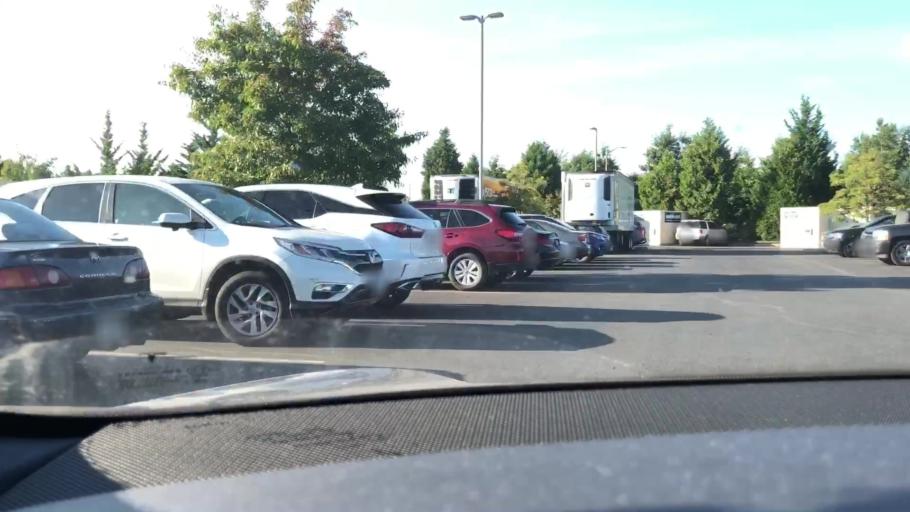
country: US
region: Washington
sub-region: Snohomish County
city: Marysville
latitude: 48.0900
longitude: -122.1903
